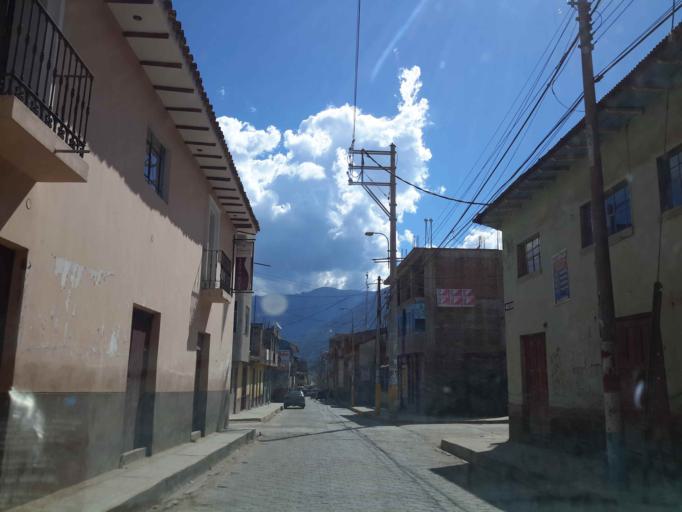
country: PE
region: Apurimac
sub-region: Provincia de Andahuaylas
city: Talavera
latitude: -13.6538
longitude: -73.4274
